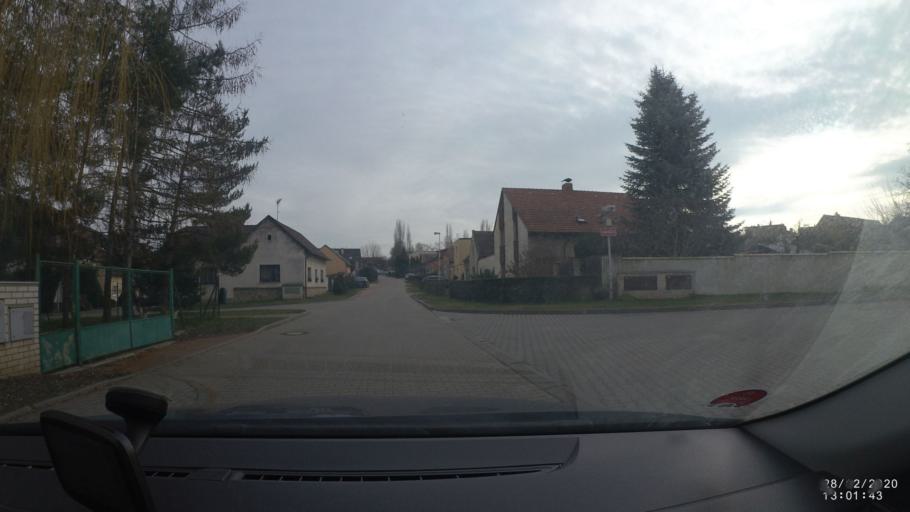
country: CZ
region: Praha
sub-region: Praha 20
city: Horni Pocernice
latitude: 50.1449
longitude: 14.6072
